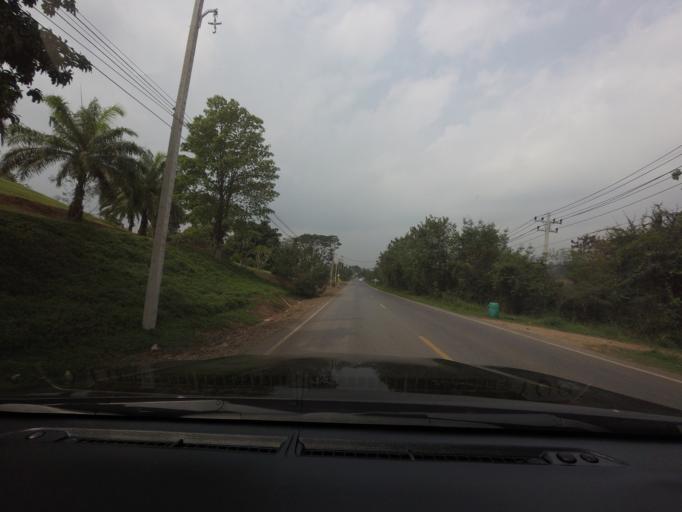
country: TH
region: Nakhon Ratchasima
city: Pak Chong
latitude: 14.4985
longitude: 101.5532
